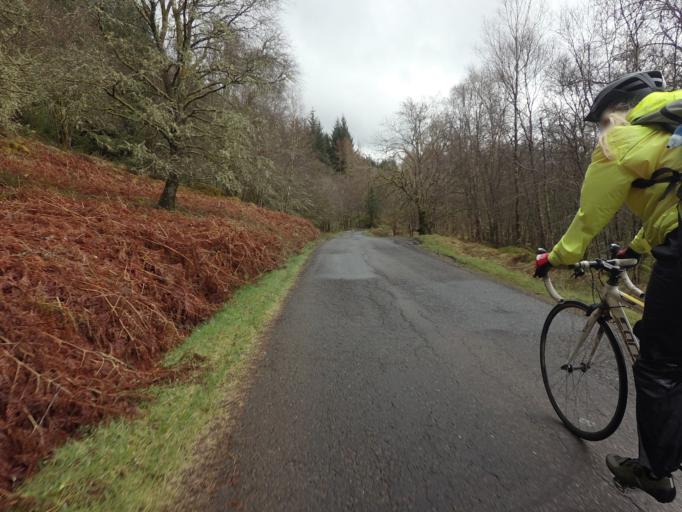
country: GB
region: Scotland
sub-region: West Dunbartonshire
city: Balloch
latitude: 56.2098
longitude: -4.5355
